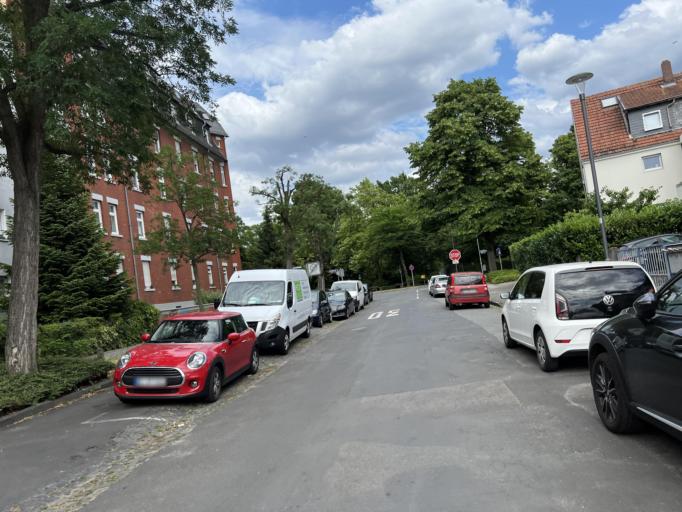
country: DE
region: Hesse
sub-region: Regierungsbezirk Darmstadt
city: Offenbach
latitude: 50.0932
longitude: 8.7612
